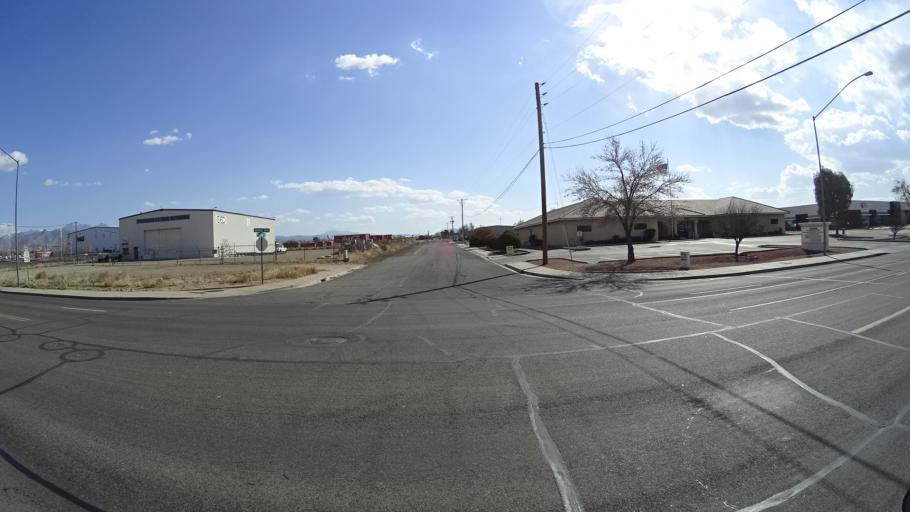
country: US
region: Arizona
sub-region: Mohave County
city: New Kingman-Butler
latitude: 35.2250
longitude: -114.0203
